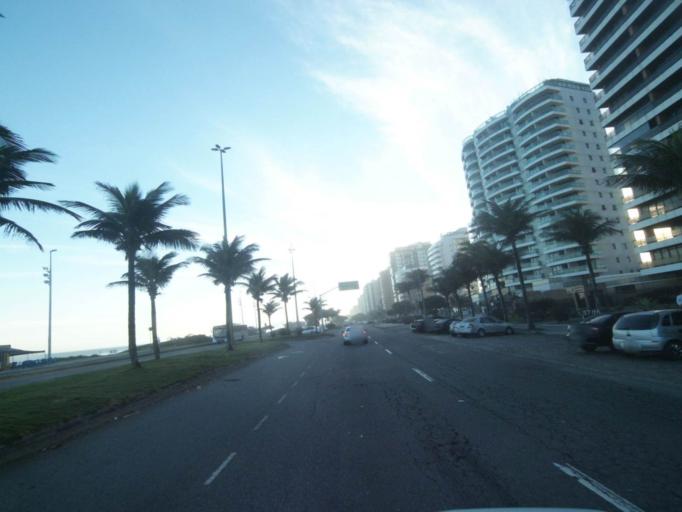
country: BR
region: Rio de Janeiro
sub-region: Rio De Janeiro
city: Rio de Janeiro
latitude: -23.0102
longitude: -43.3519
